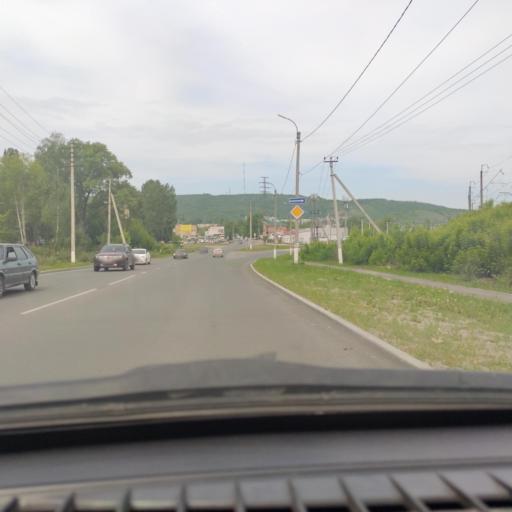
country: RU
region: Samara
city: Zhigulevsk
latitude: 53.4064
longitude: 49.4900
